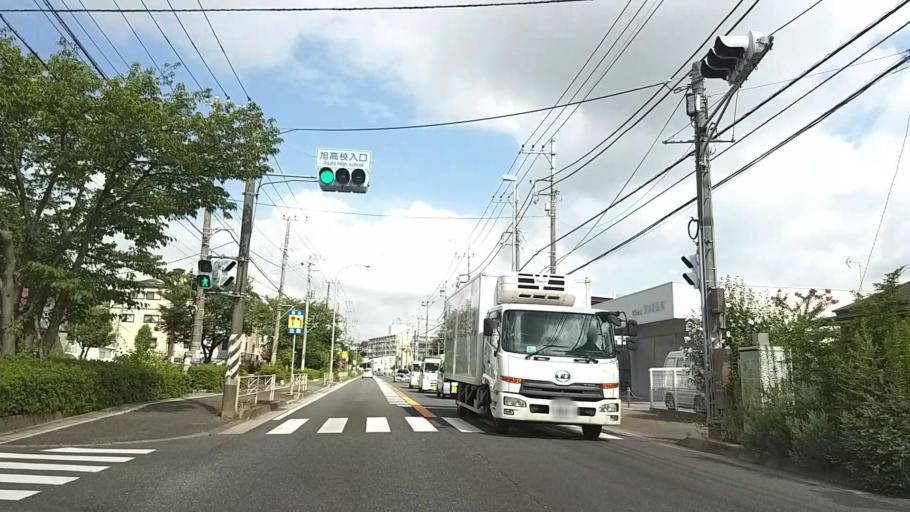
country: JP
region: Kanagawa
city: Minami-rinkan
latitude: 35.4913
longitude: 139.5136
